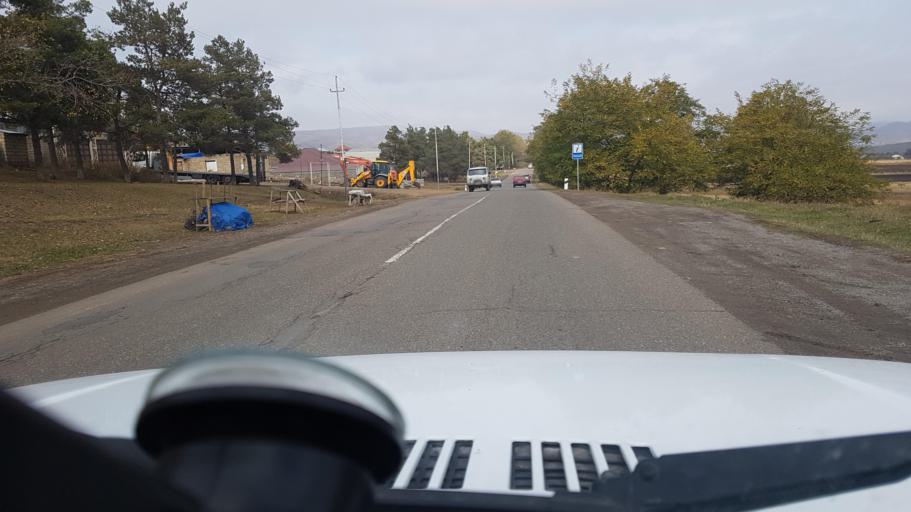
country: AZ
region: Gadabay Rayon
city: Ariqdam
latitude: 40.6392
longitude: 45.8130
